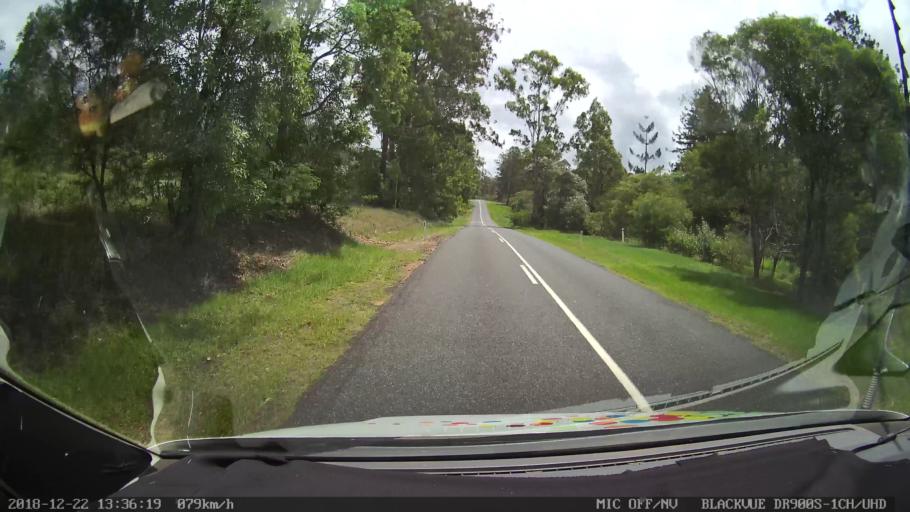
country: AU
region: New South Wales
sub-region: Clarence Valley
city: Coutts Crossing
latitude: -29.8792
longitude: 152.7962
